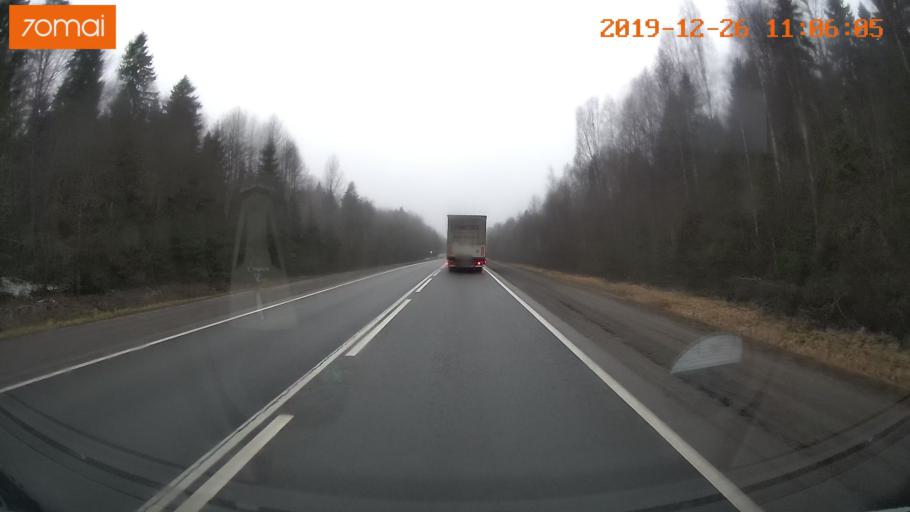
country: RU
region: Vologda
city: Molochnoye
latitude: 59.1436
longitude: 39.3283
